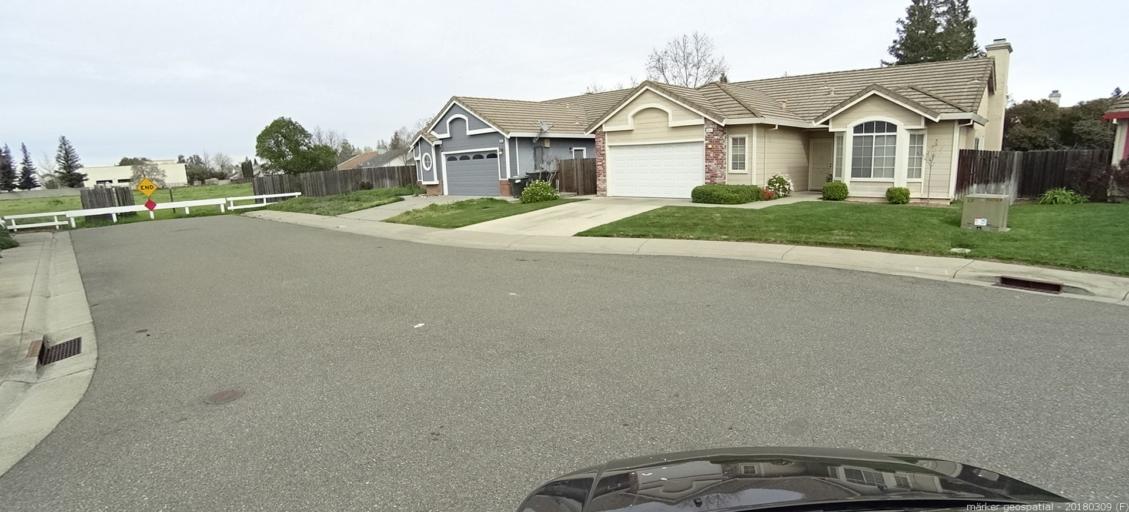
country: US
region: California
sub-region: Sacramento County
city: Vineyard
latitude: 38.4628
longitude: -121.3704
